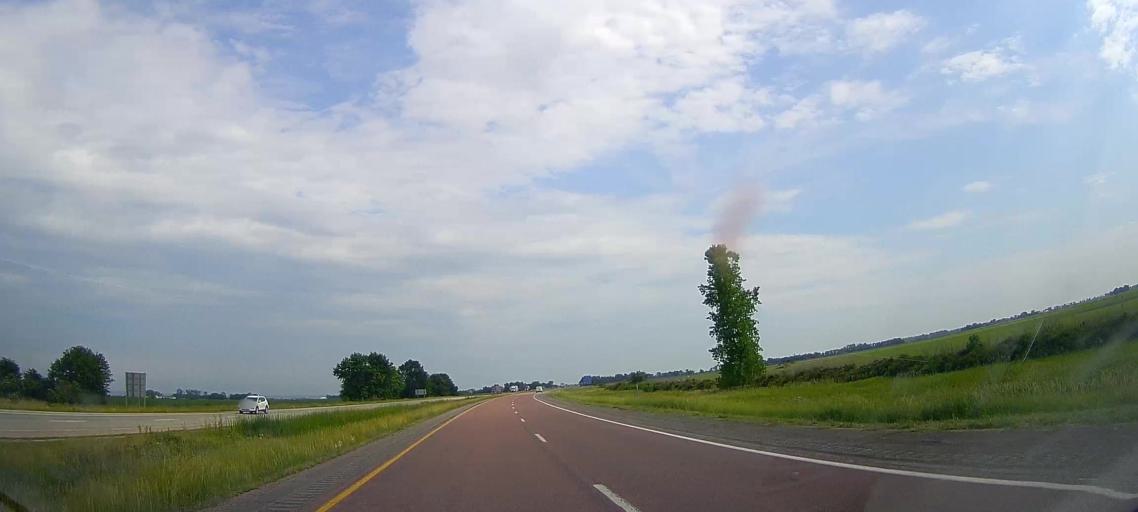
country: US
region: Iowa
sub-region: Monona County
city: Onawa
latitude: 42.0090
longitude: -96.1181
